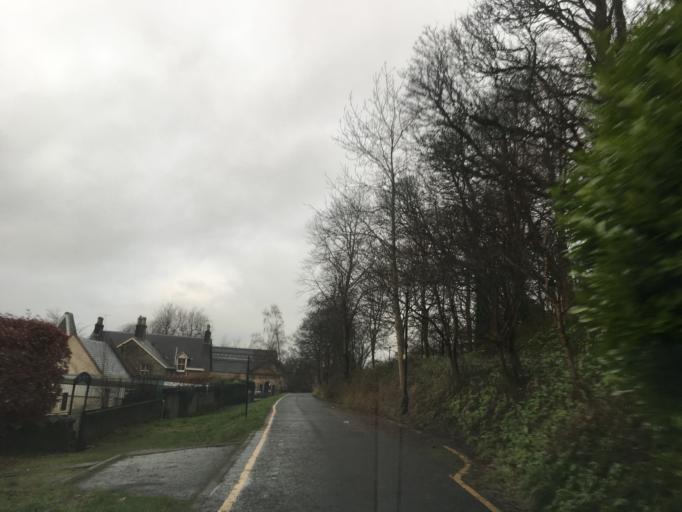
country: GB
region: Scotland
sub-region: Stirling
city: Stirling
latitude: 56.1190
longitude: -3.9435
